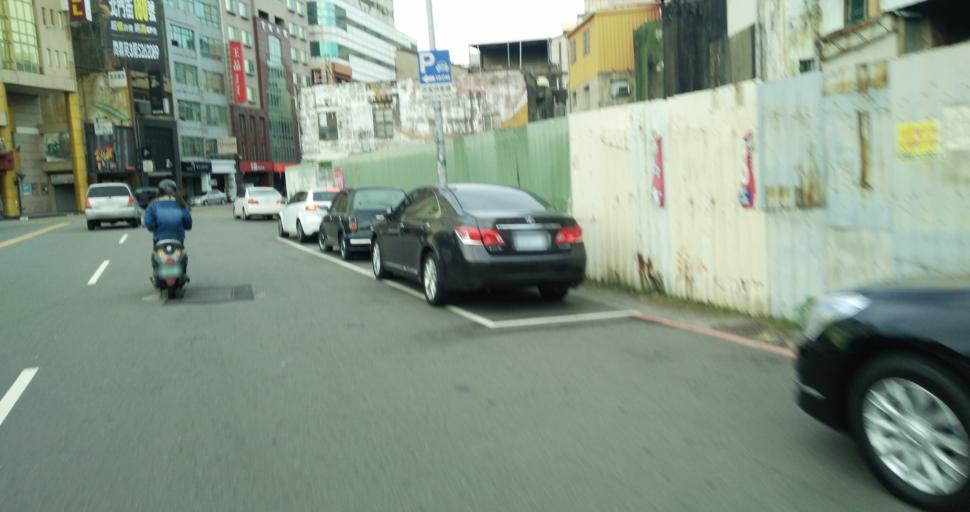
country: TW
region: Taiwan
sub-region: Hsinchu
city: Hsinchu
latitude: 24.8050
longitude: 120.9611
